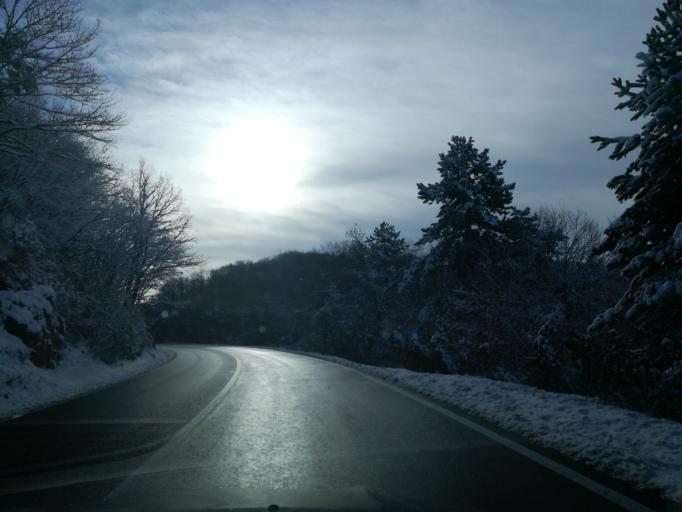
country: RO
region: Brasov
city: Brasov
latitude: 45.6406
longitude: 25.5614
